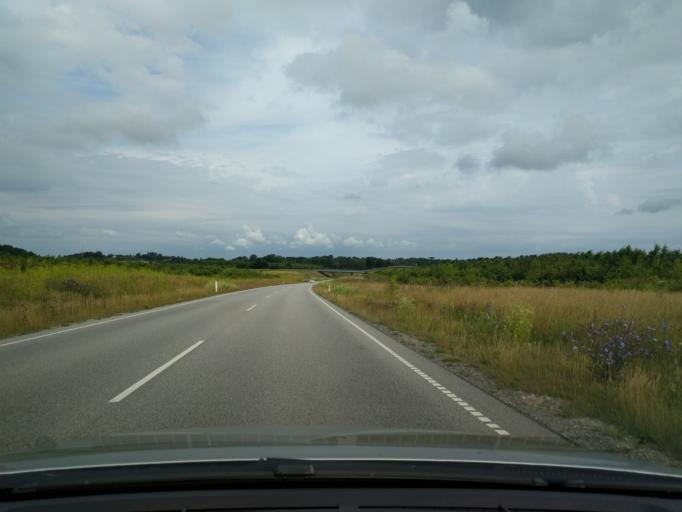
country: DK
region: Zealand
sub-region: Naestved Kommune
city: Naestved
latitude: 55.2142
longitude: 11.8072
